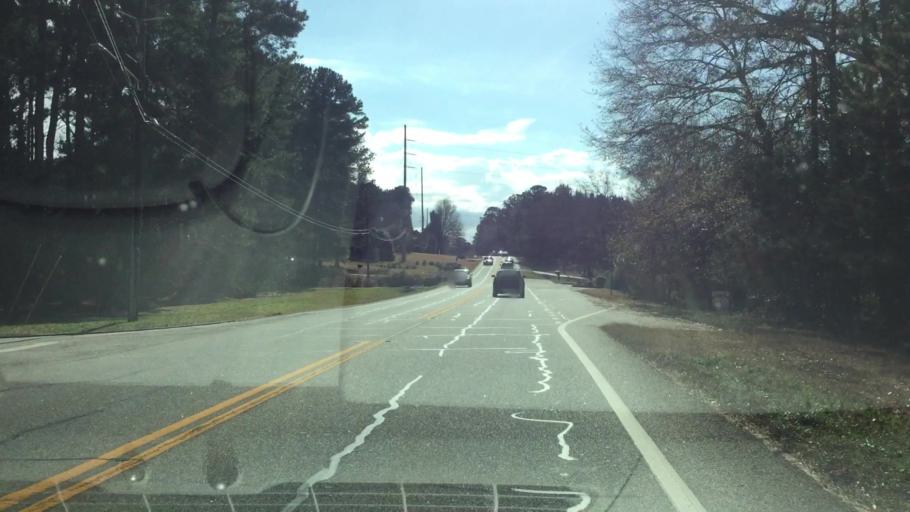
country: US
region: Georgia
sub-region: Henry County
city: McDonough
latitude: 33.4626
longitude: -84.1417
